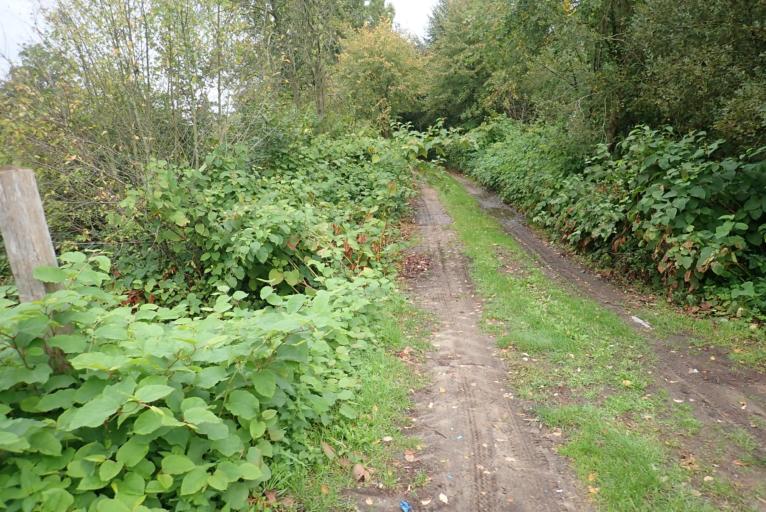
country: BE
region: Flanders
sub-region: Provincie Antwerpen
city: Zandhoven
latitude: 51.2119
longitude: 4.6978
